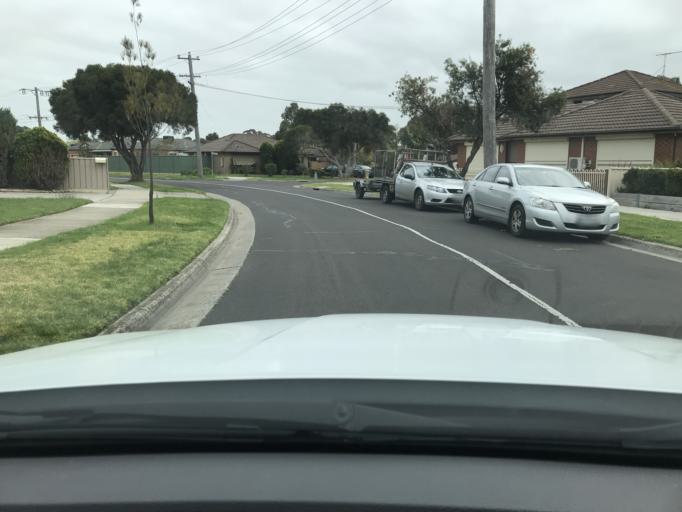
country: AU
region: Victoria
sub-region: Hume
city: Craigieburn
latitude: -37.6022
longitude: 144.9283
